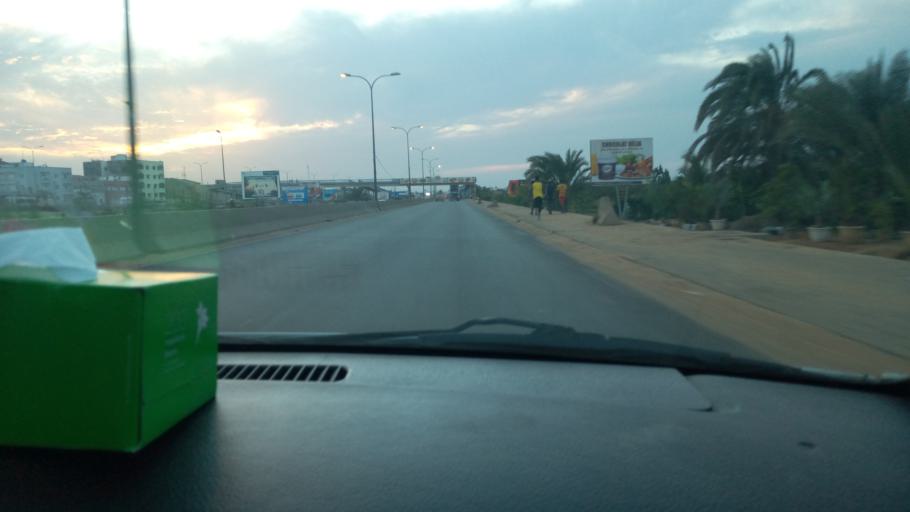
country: SN
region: Dakar
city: Pikine
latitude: 14.7466
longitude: -17.4126
